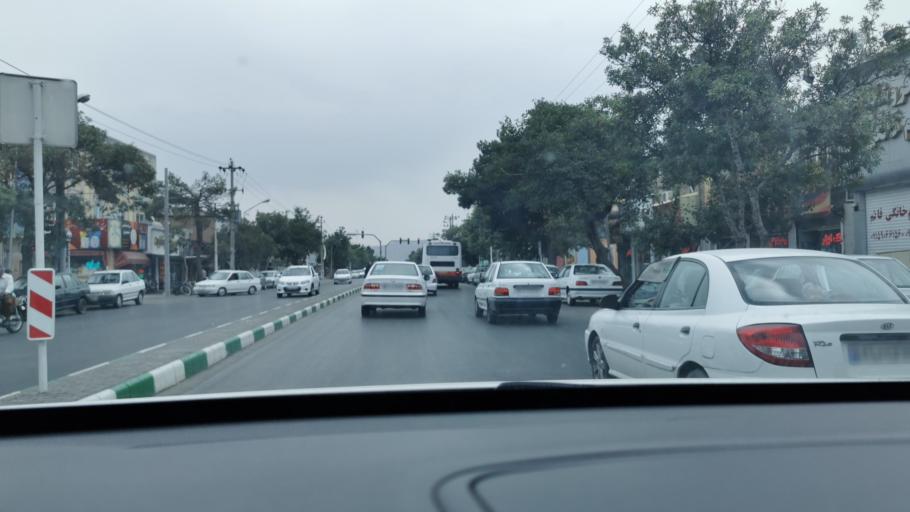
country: IR
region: Razavi Khorasan
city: Mashhad
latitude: 36.3185
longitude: 59.6186
